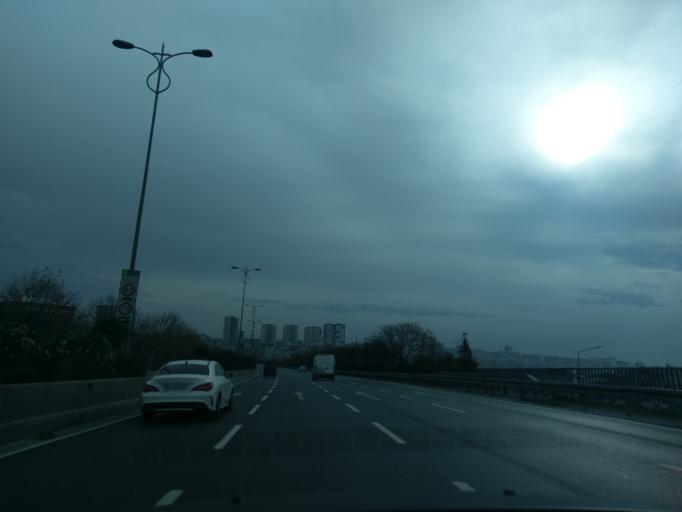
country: TR
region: Istanbul
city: Mahmutbey
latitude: 41.0580
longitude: 28.8453
